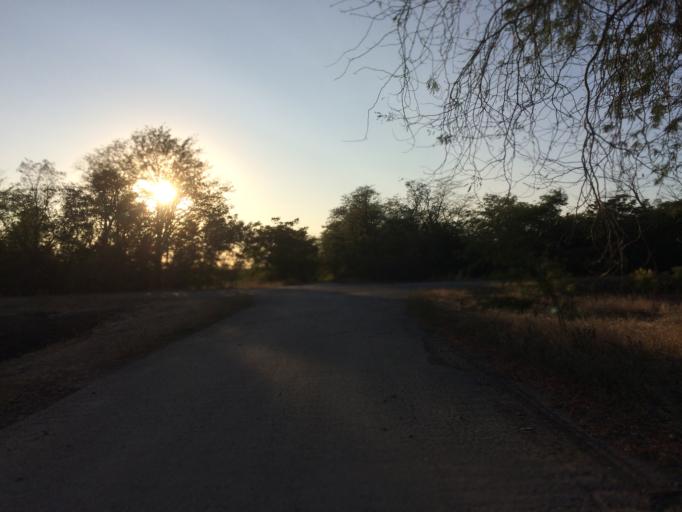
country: RU
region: Rostov
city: Gigant
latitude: 46.5094
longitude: 41.1922
